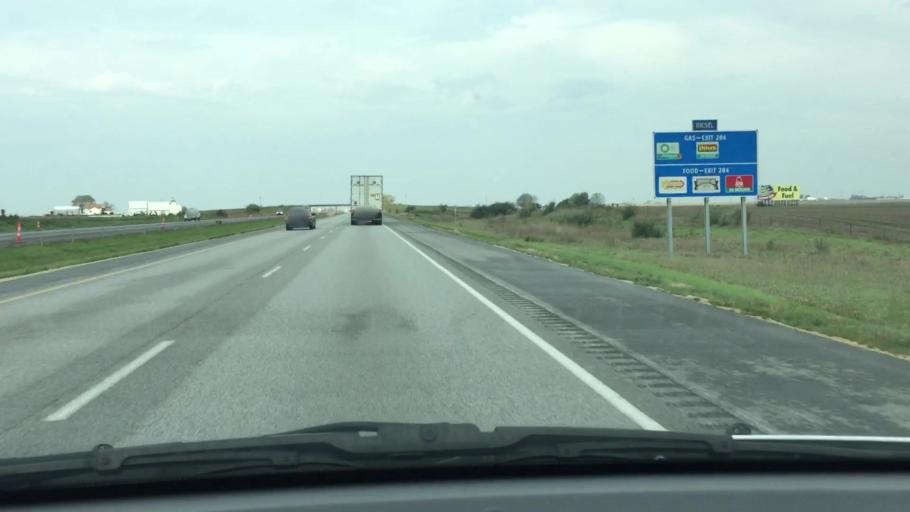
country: US
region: Iowa
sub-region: Scott County
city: Walcott
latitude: 41.6071
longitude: -90.7360
